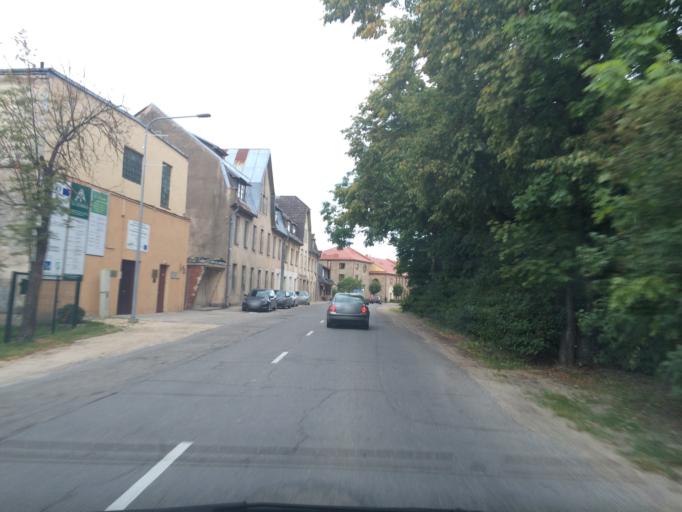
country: LV
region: Plavinu
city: Plavinas
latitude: 56.6154
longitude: 25.7199
